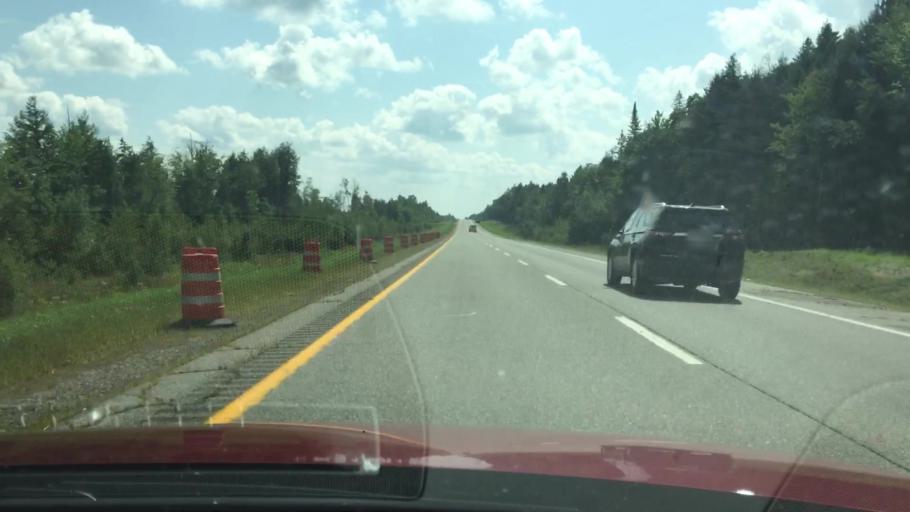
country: US
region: Maine
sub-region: Penobscot County
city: Medway
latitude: 45.5453
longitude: -68.5528
